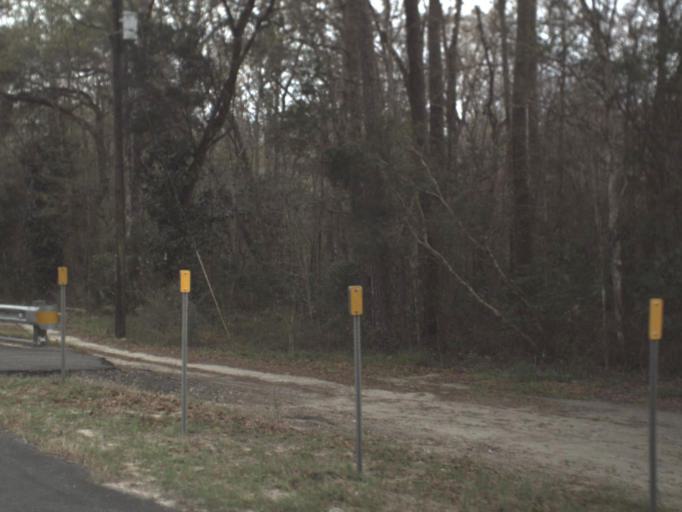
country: US
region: Florida
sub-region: Leon County
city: Woodville
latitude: 30.2397
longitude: -84.2707
